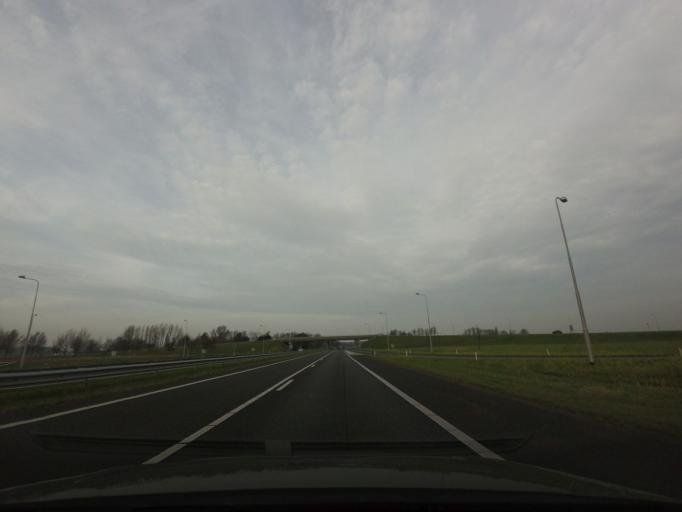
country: NL
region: North Holland
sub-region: Gemeente Medemblik
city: Opperdoes
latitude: 52.7202
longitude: 5.0254
